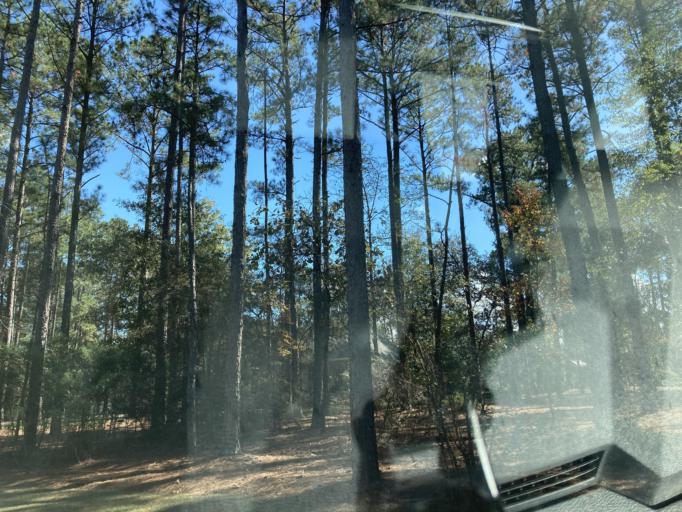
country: US
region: Mississippi
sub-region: Lamar County
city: West Hattiesburg
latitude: 31.2517
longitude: -89.3898
